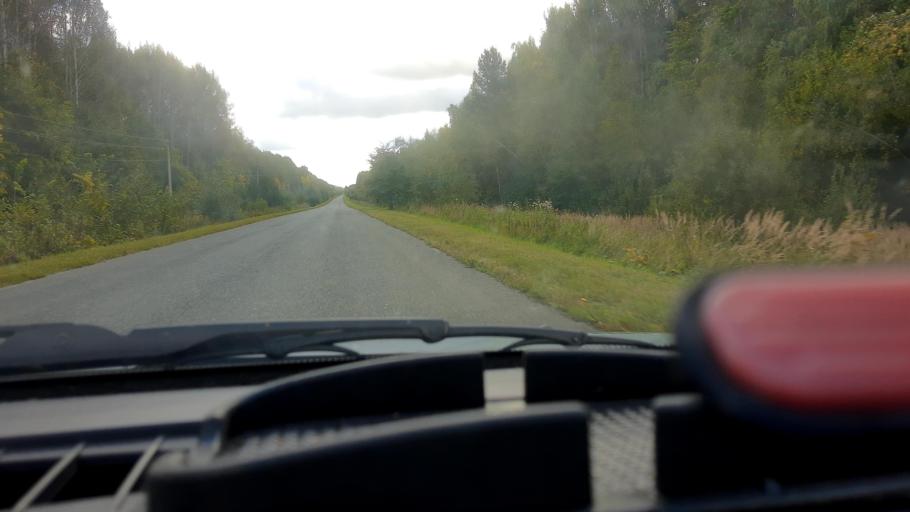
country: RU
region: Mariy-El
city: Kilemary
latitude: 56.9194
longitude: 46.7175
